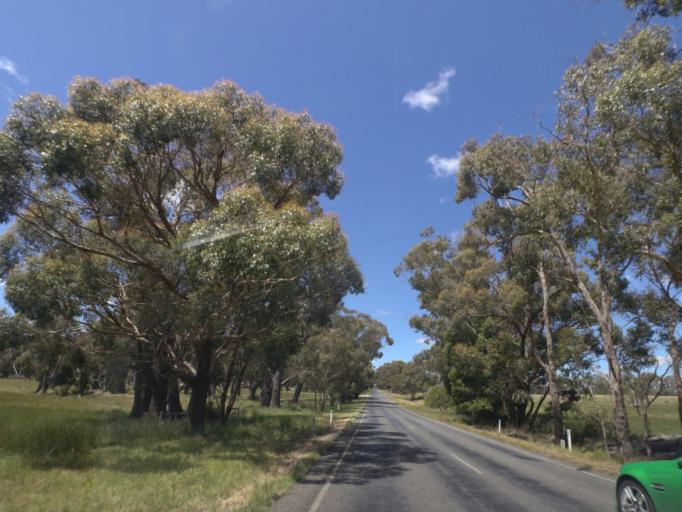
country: AU
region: Victoria
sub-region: Mount Alexander
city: Castlemaine
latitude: -37.3176
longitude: 144.2144
